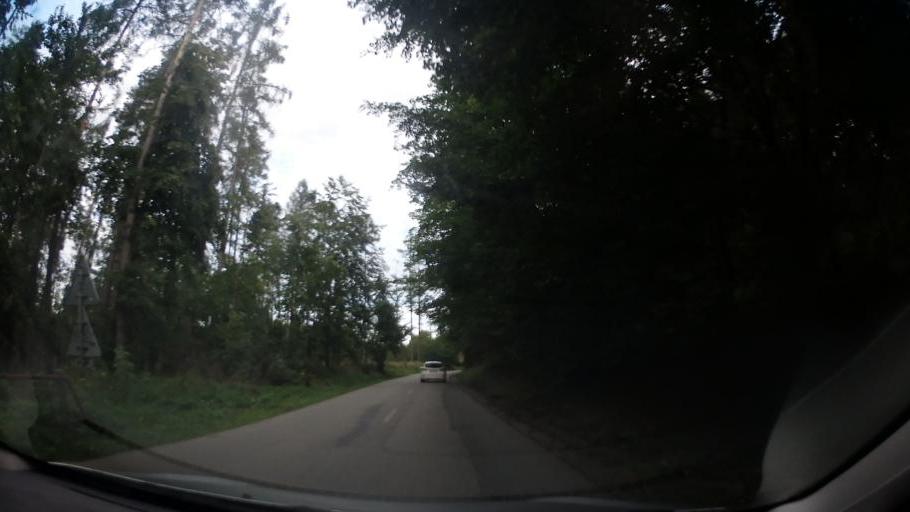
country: CZ
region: Olomoucky
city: Horni Stepanov
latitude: 49.5370
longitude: 16.7213
